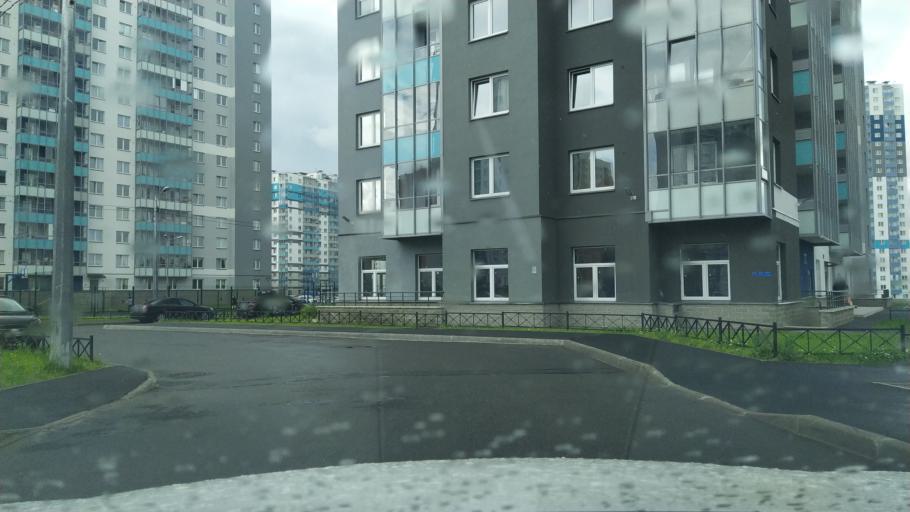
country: RU
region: Leningrad
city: Murino
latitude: 60.0339
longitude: 30.4595
